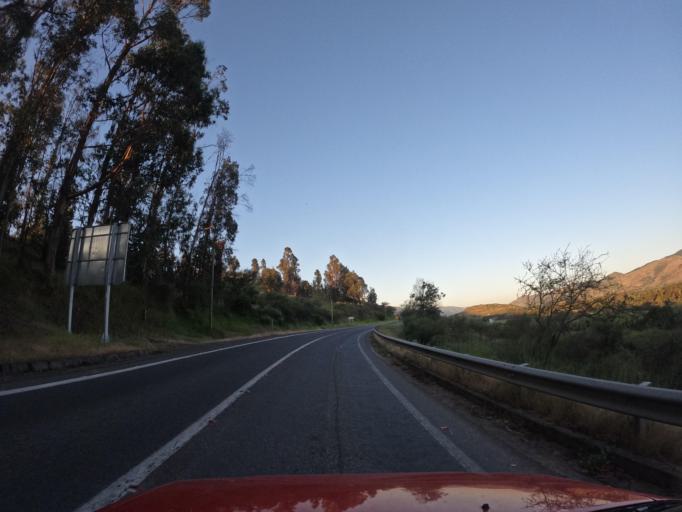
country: CL
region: Maule
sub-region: Provincia de Talca
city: Talca
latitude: -35.0882
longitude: -71.6462
